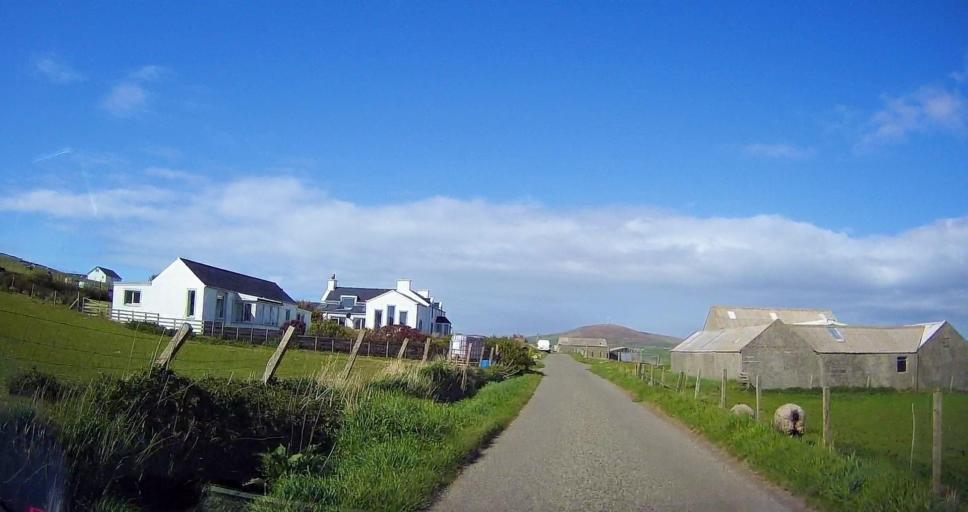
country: GB
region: Scotland
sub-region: Shetland Islands
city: Sandwick
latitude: 59.9064
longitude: -1.3348
